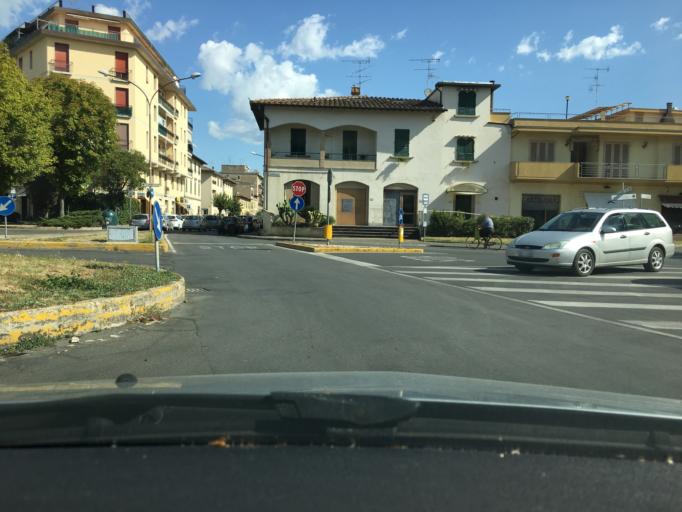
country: IT
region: Tuscany
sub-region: Province of Florence
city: Castelfiorentino
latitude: 43.6013
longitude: 10.9668
